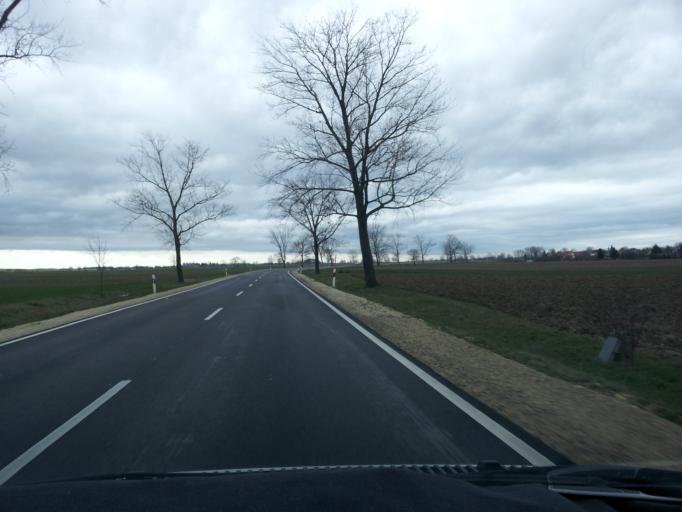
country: HU
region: Gyor-Moson-Sopron
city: Beled
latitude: 47.4608
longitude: 17.1065
